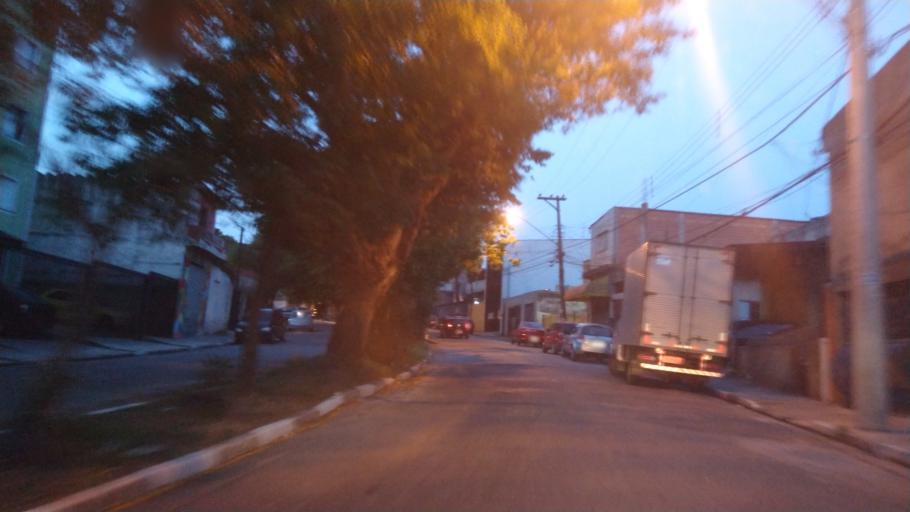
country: BR
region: Sao Paulo
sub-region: Aruja
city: Aruja
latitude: -23.4160
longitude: -46.4044
